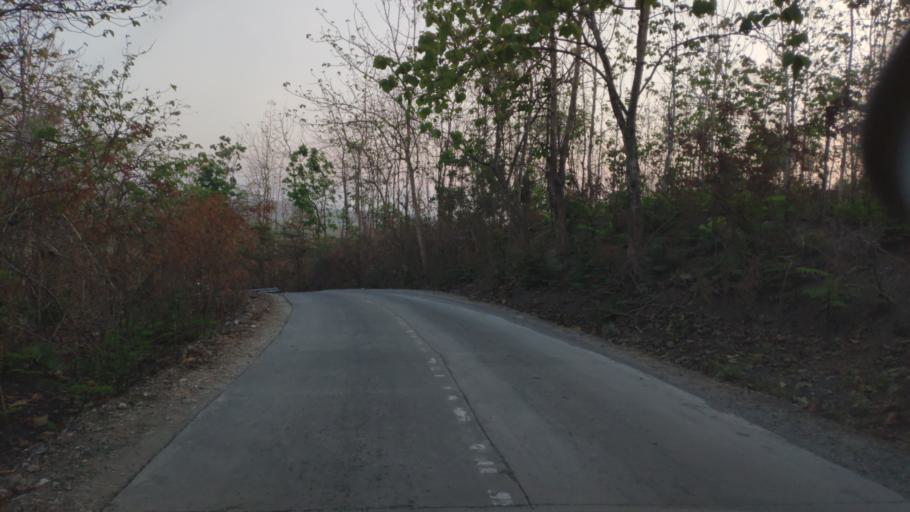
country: ID
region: Central Java
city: Klopoduwur
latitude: -7.0496
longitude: 111.4056
